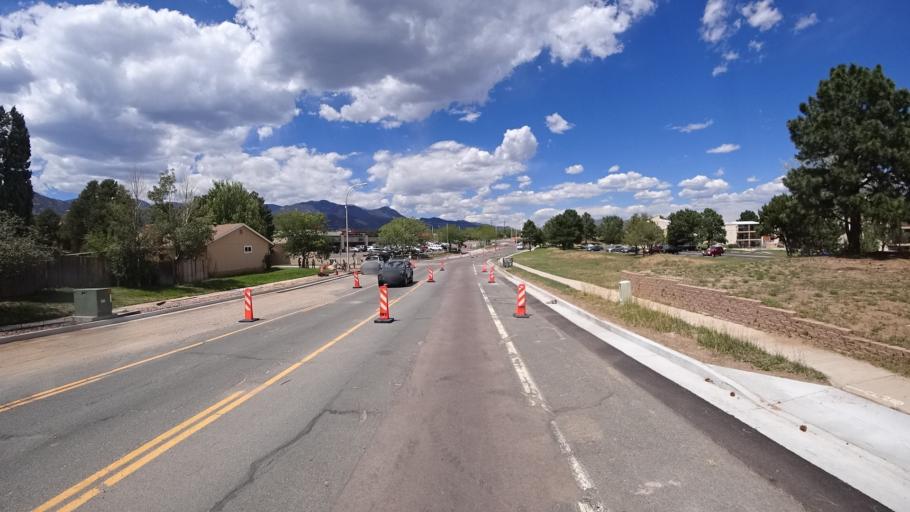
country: US
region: Colorado
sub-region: El Paso County
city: Stratmoor
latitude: 38.7880
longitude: -104.8191
